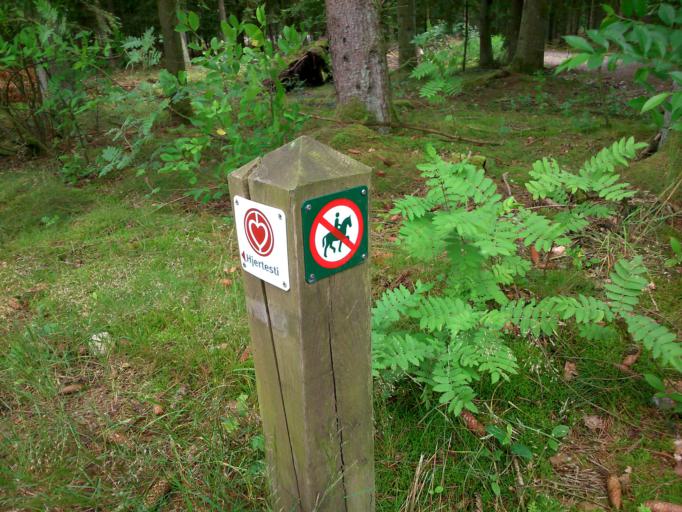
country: DK
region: Central Jutland
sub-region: Ringkobing-Skjern Kommune
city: Skjern
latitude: 55.9499
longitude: 8.5248
